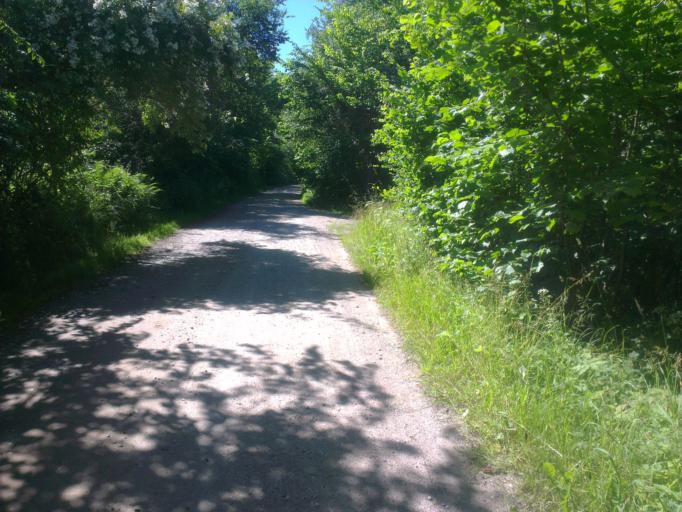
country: DK
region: Capital Region
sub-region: Halsnaes Kommune
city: Liseleje
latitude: 55.9311
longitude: 11.9392
